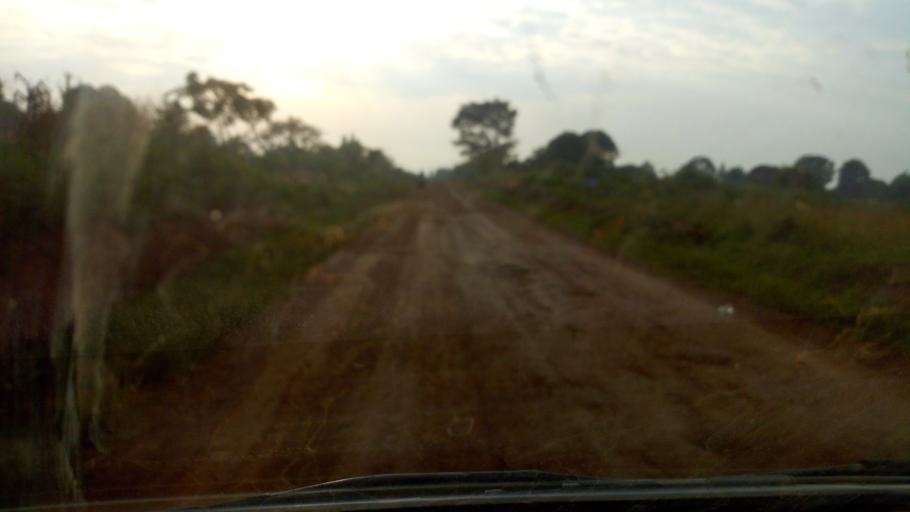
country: UG
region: Western Region
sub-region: Masindi District
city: Masindi
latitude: 1.6736
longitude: 31.7619
